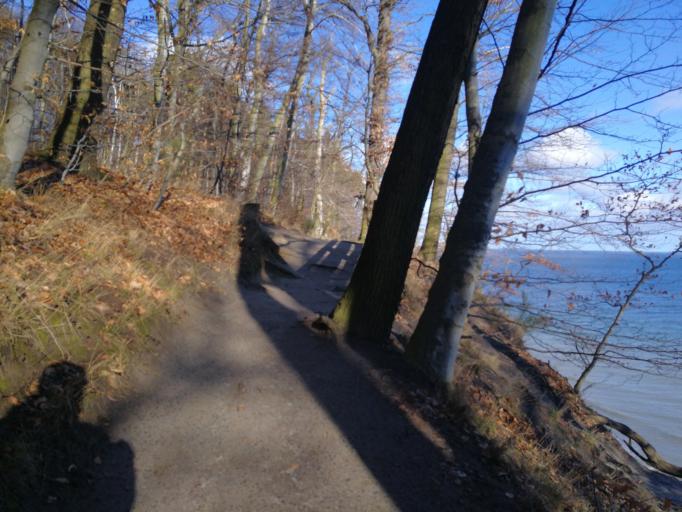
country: PL
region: Pomeranian Voivodeship
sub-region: Sopot
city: Sopot
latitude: 54.4842
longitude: 18.5662
